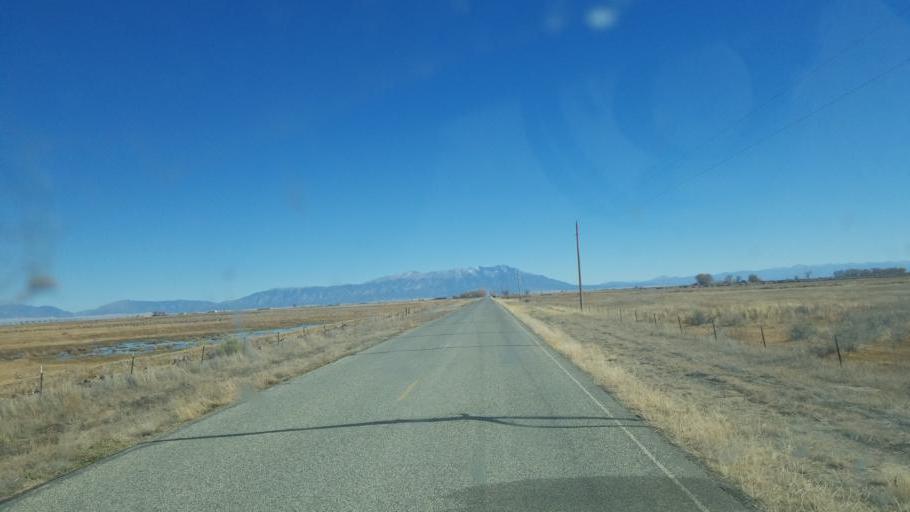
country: US
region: Colorado
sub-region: Rio Grande County
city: Monte Vista
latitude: 37.5743
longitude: -105.9918
